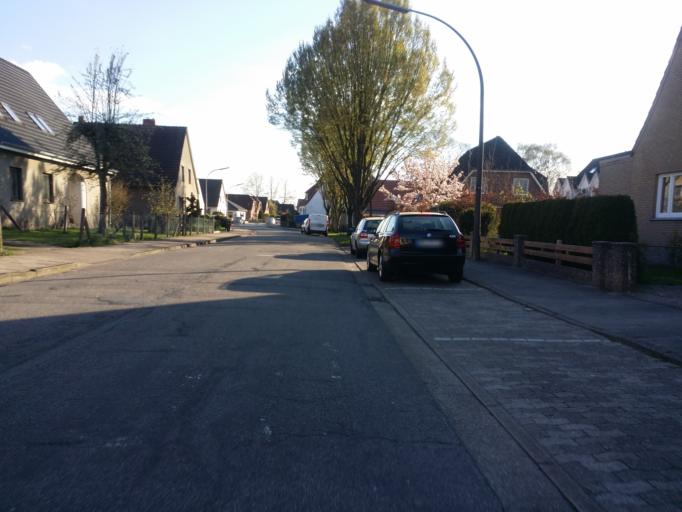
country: DE
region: Lower Saxony
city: Delmenhorst
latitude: 53.0241
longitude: 8.6230
